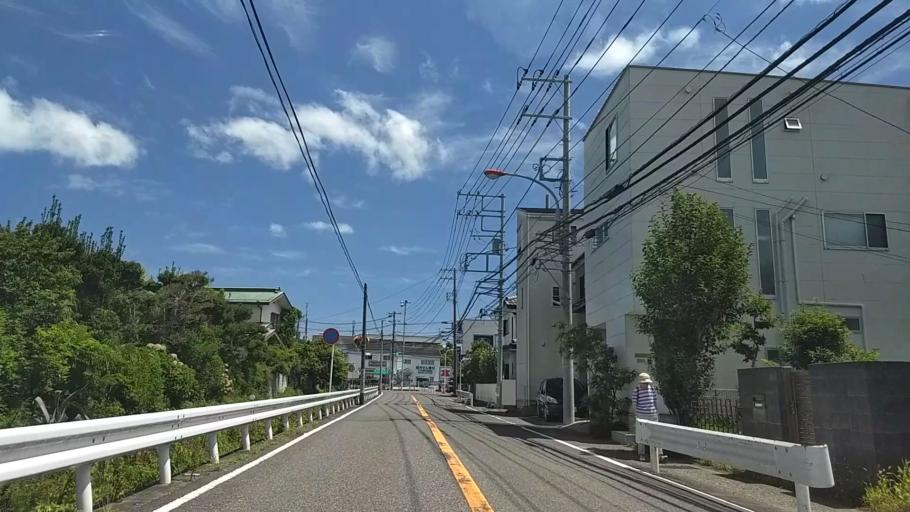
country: JP
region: Kanagawa
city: Kamakura
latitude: 35.3426
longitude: 139.5359
